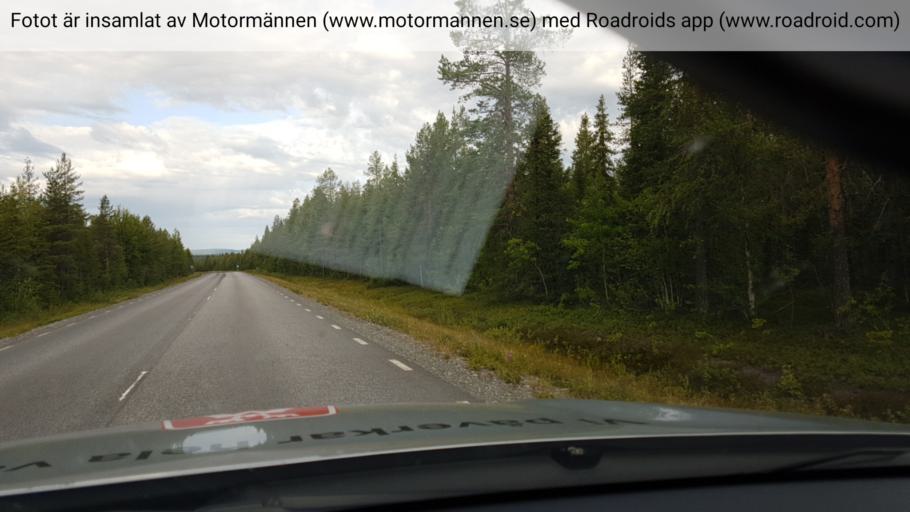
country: SE
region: Vaesterbotten
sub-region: Skelleftea Kommun
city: Storvik
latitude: 65.3686
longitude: 20.4027
